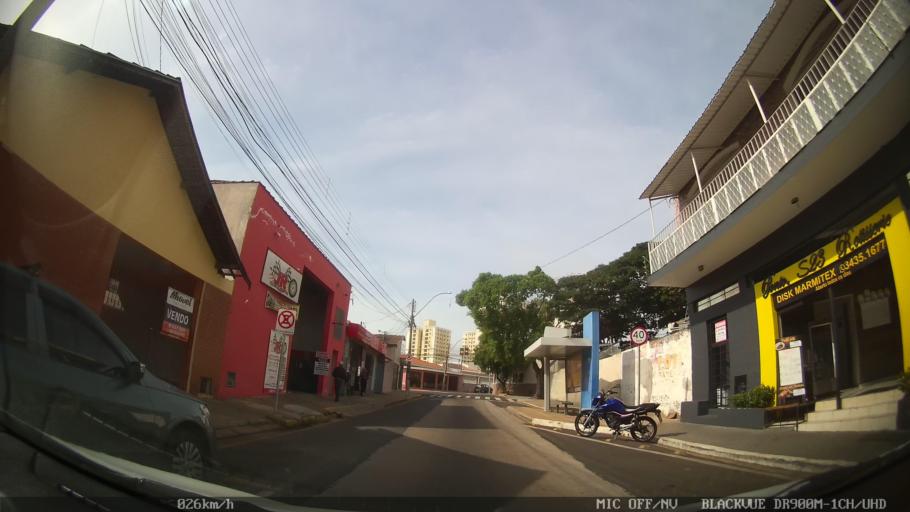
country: BR
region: Sao Paulo
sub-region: Piracicaba
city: Piracicaba
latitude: -22.7391
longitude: -47.6587
